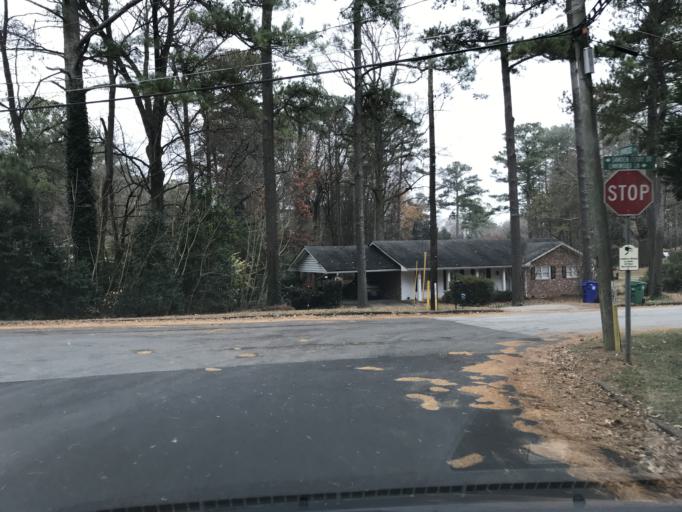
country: US
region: Georgia
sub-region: DeKalb County
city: Clarkston
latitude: 33.8241
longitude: -84.2571
